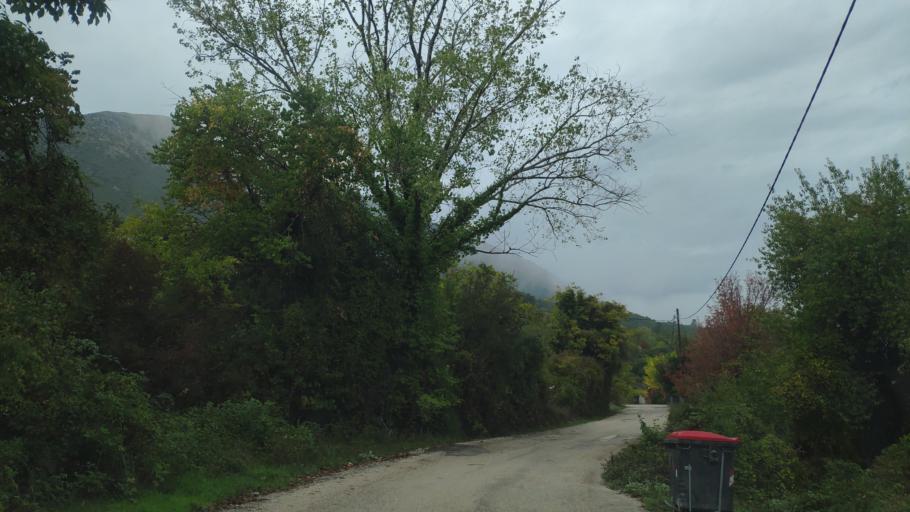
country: GR
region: Epirus
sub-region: Nomos Thesprotias
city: Paramythia
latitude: 39.4627
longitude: 20.6736
